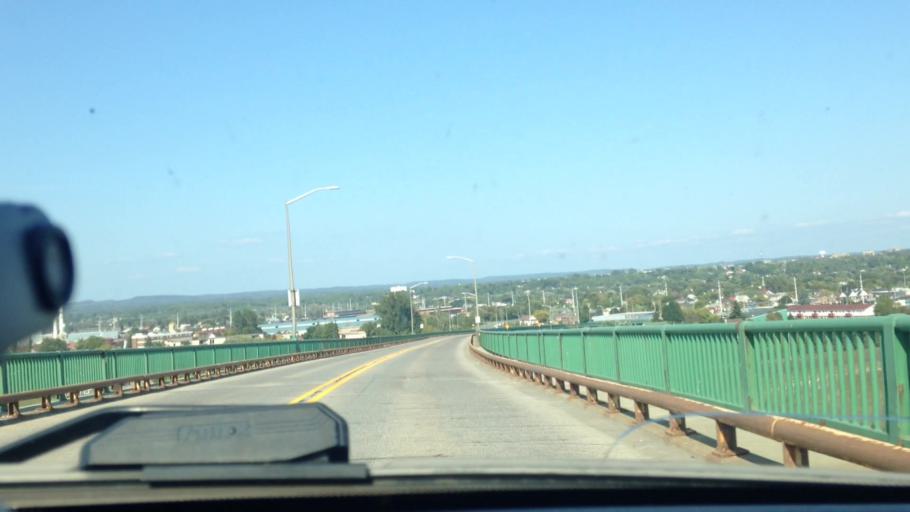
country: US
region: Michigan
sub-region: Chippewa County
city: Sault Ste. Marie
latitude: 46.5146
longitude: -84.3581
